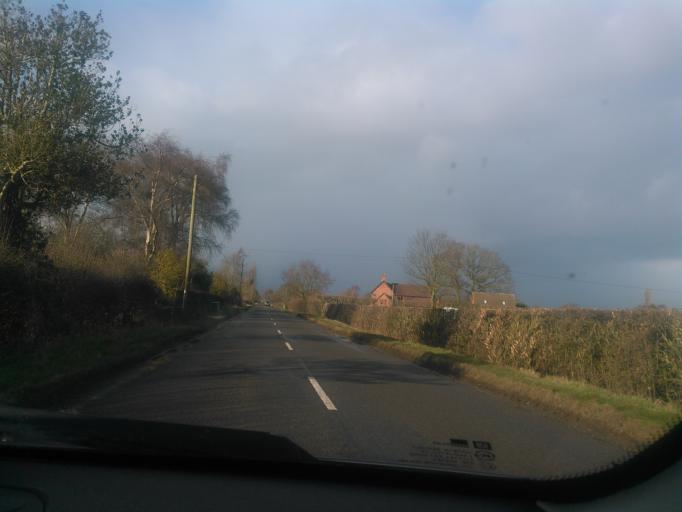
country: GB
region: England
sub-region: Shropshire
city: Shawbury
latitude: 52.7767
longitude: -2.6384
